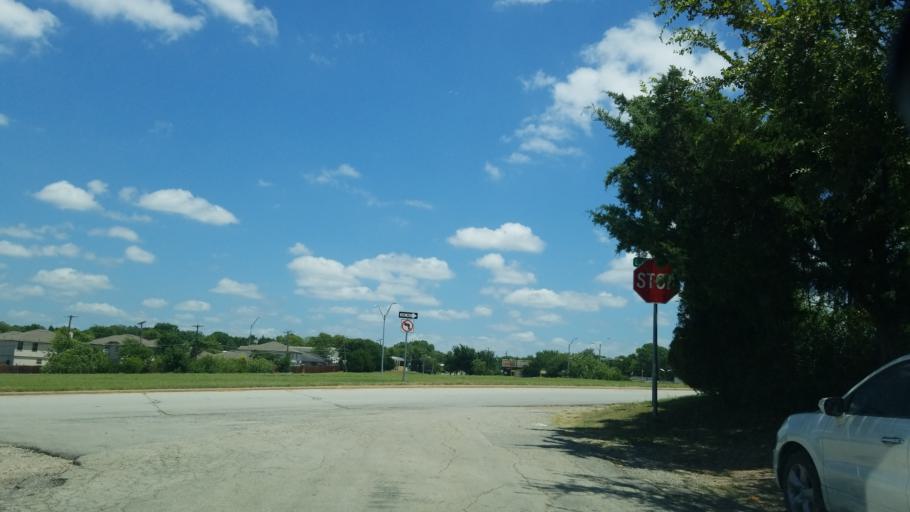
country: US
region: Texas
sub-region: Dallas County
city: Hutchins
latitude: 32.7344
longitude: -96.7148
